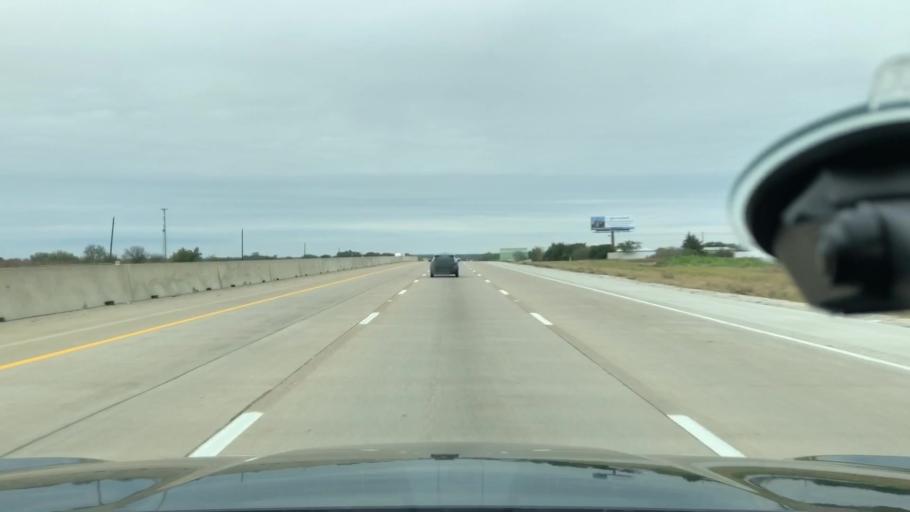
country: US
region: Texas
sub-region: Ellis County
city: Waxahachie
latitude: 32.3261
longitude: -96.8593
